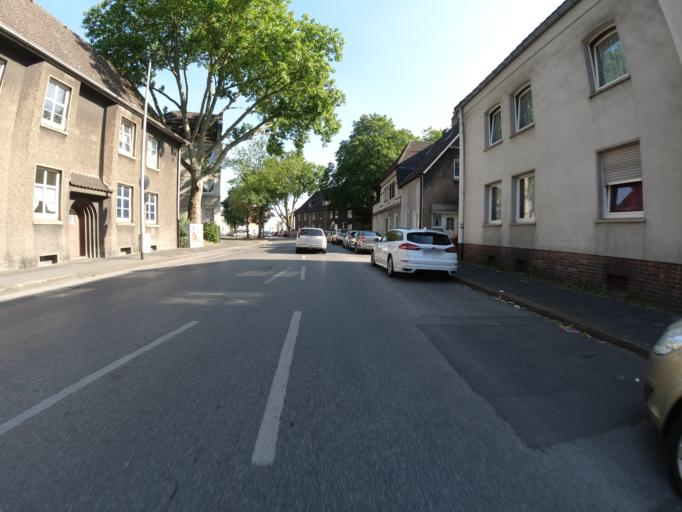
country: DE
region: North Rhine-Westphalia
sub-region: Regierungsbezirk Dusseldorf
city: Hochfeld
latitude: 51.4063
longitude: 6.7229
